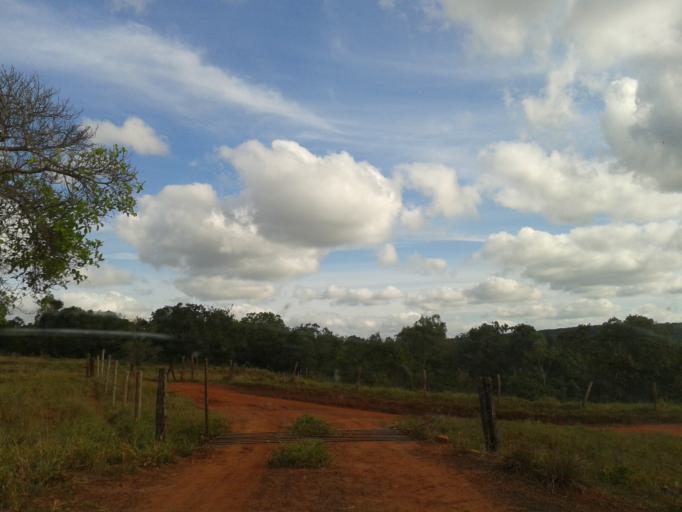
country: BR
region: Minas Gerais
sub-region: Campina Verde
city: Campina Verde
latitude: -19.4426
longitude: -49.7332
